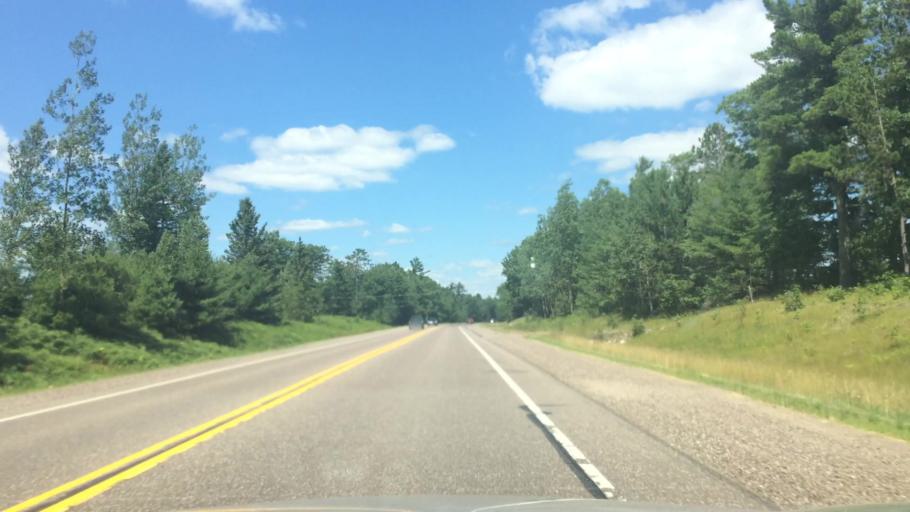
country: US
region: Wisconsin
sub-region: Vilas County
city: Lac du Flambeau
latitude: 45.9450
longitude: -89.6984
